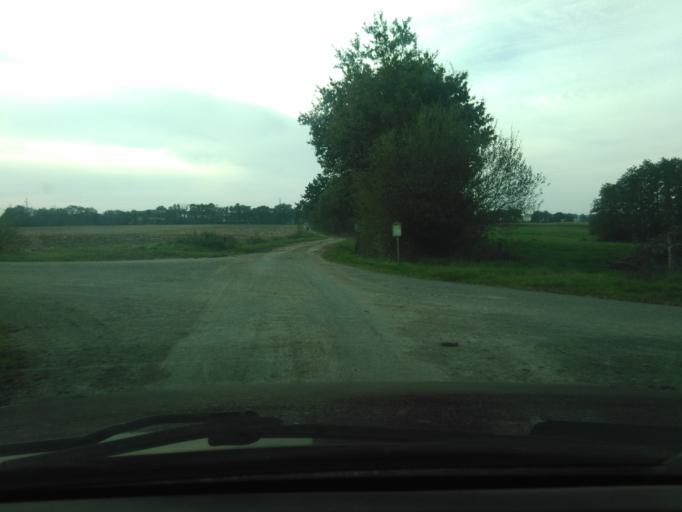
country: FR
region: Pays de la Loire
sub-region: Departement de la Vendee
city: Dompierre-sur-Yon
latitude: 46.7174
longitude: -1.4163
